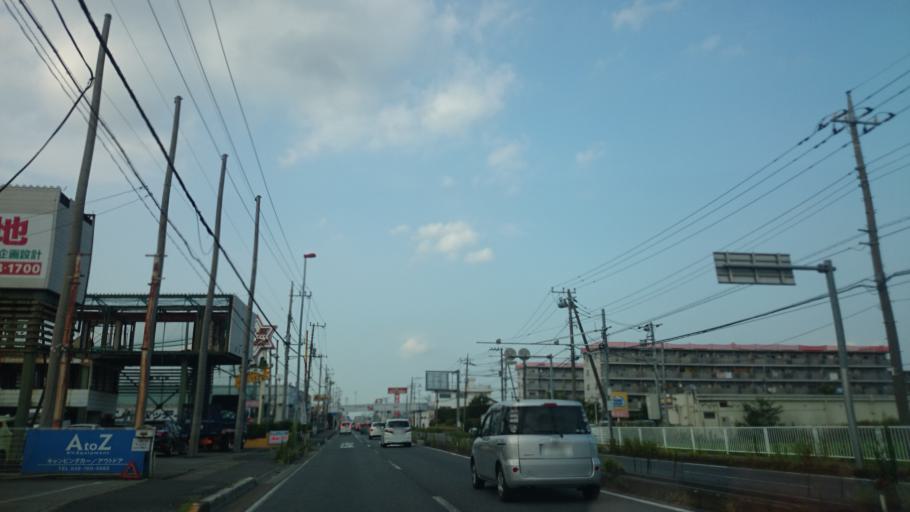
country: JP
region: Saitama
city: Kasukabe
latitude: 35.9582
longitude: 139.7287
